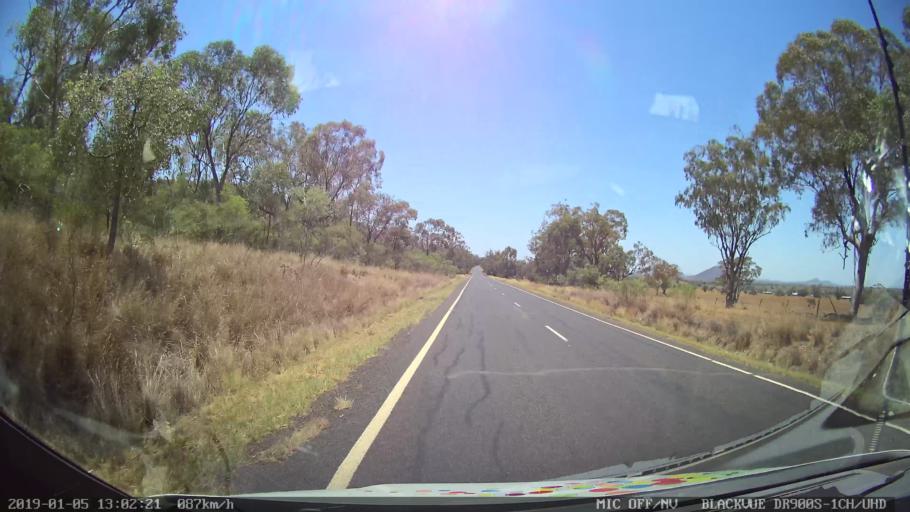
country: AU
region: New South Wales
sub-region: Narrabri
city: Boggabri
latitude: -31.1154
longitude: 149.8103
